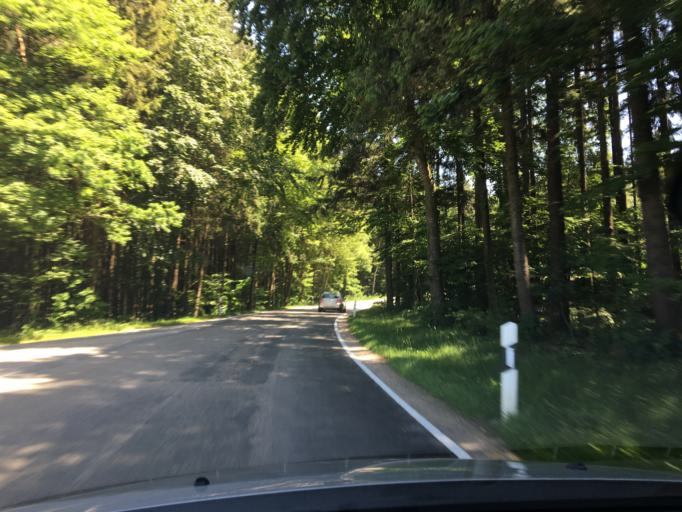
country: DE
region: Bavaria
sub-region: Upper Bavaria
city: Halsbach
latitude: 48.1008
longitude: 12.7201
